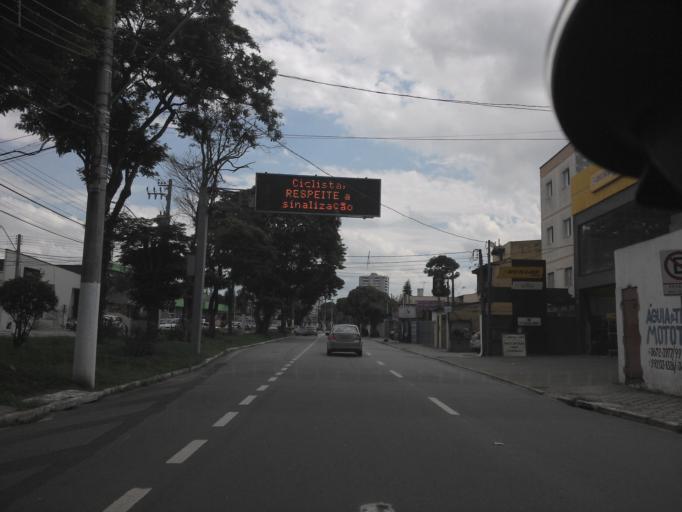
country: BR
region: Sao Paulo
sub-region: Taubate
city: Taubate
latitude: -23.0160
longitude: -45.5514
